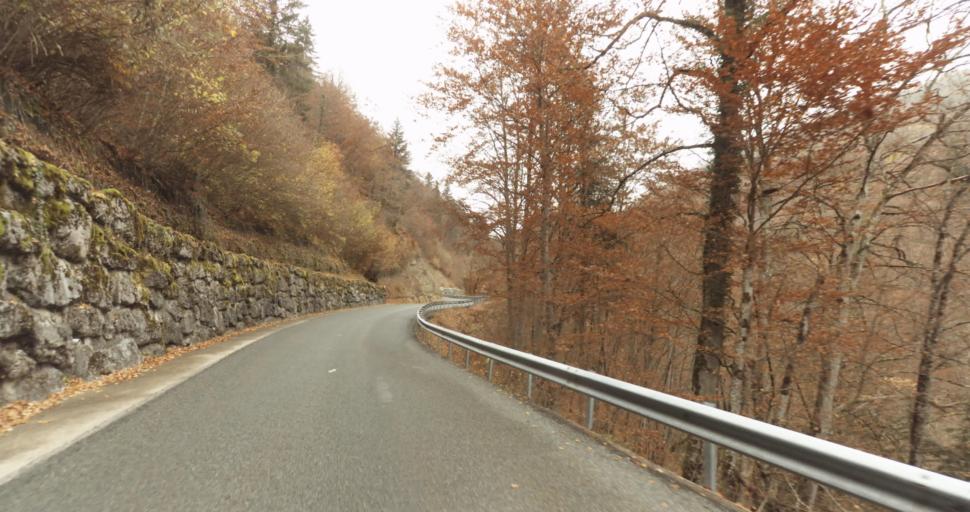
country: FR
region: Rhone-Alpes
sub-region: Departement de la Haute-Savoie
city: Doussard
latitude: 45.7844
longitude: 6.2591
